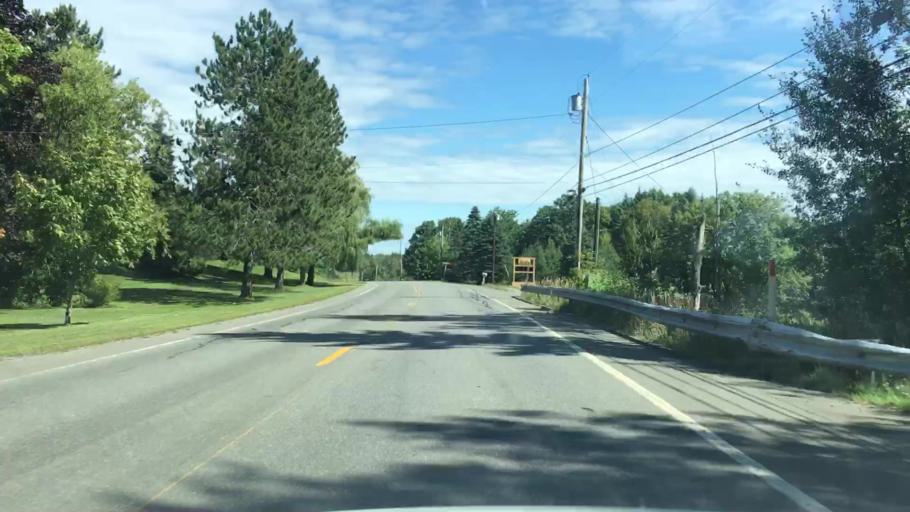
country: US
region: Maine
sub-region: Penobscot County
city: Dexter
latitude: 45.0687
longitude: -69.2394
